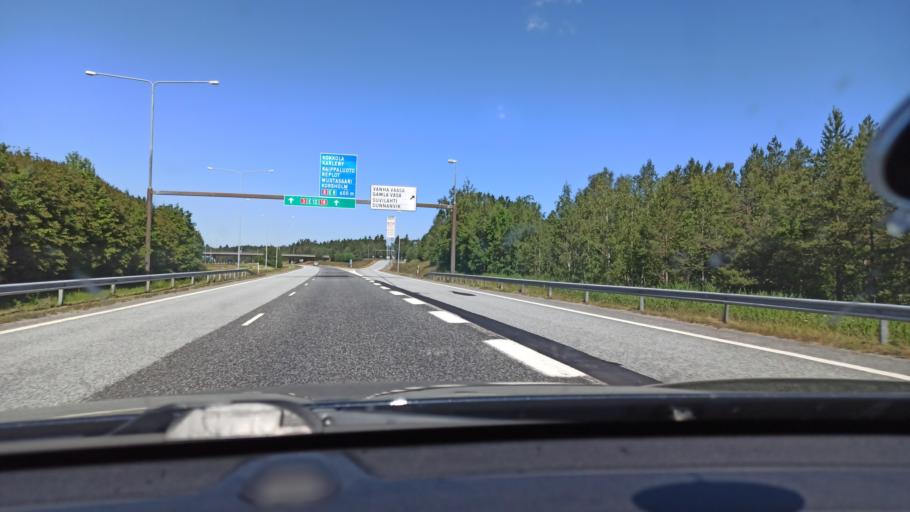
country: FI
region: Ostrobothnia
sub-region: Vaasa
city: Teeriniemi
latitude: 63.0672
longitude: 21.7025
